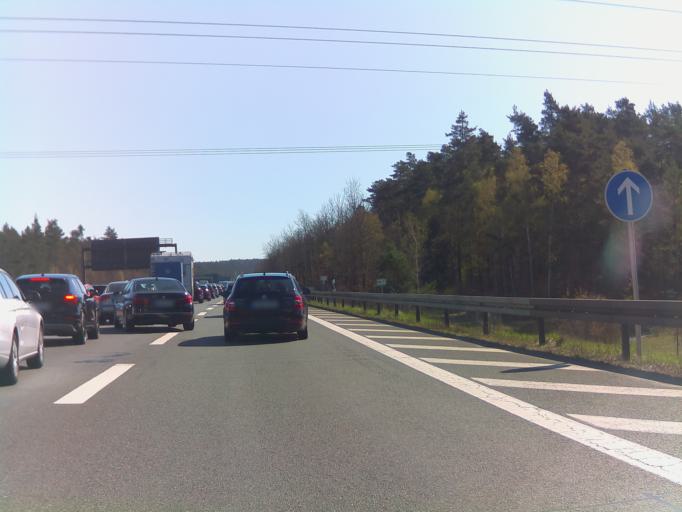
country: DE
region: Bavaria
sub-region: Regierungsbezirk Mittelfranken
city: Feucht
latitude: 49.3965
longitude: 11.2067
